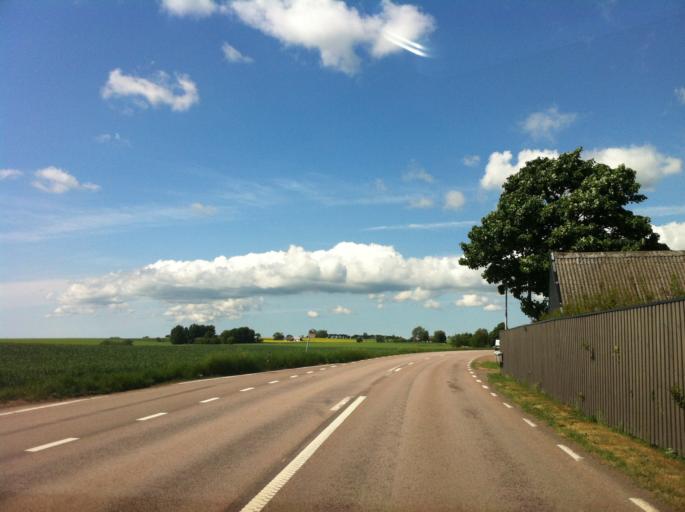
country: SE
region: Skane
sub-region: Helsingborg
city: Glumslov
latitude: 55.9650
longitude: 12.8919
